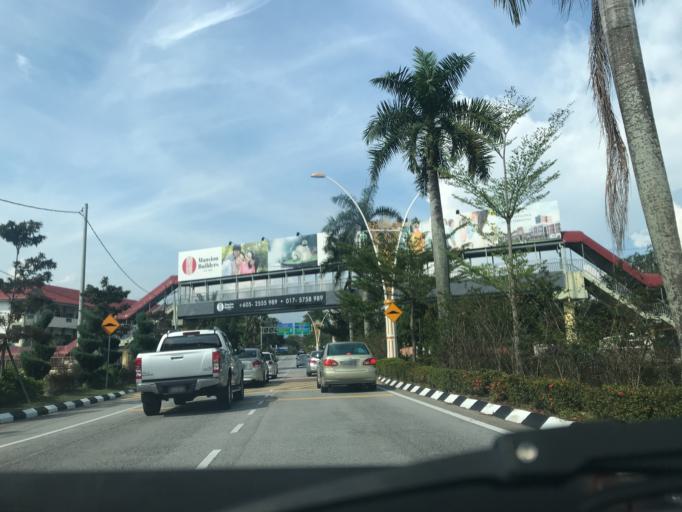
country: MY
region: Perak
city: Ipoh
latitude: 4.5962
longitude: 101.1014
